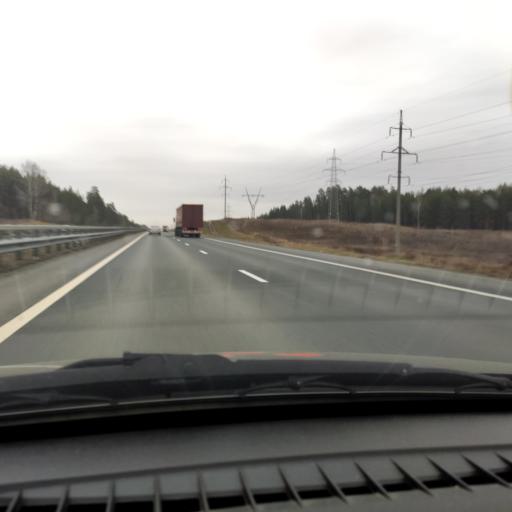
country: RU
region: Samara
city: Povolzhskiy
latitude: 53.5169
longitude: 49.7431
